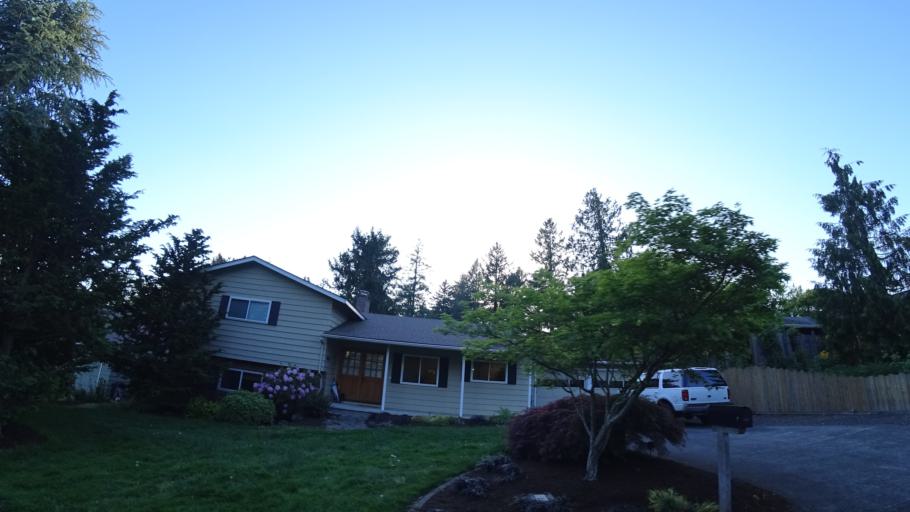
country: US
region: Oregon
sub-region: Washington County
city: West Slope
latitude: 45.4911
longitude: -122.7698
